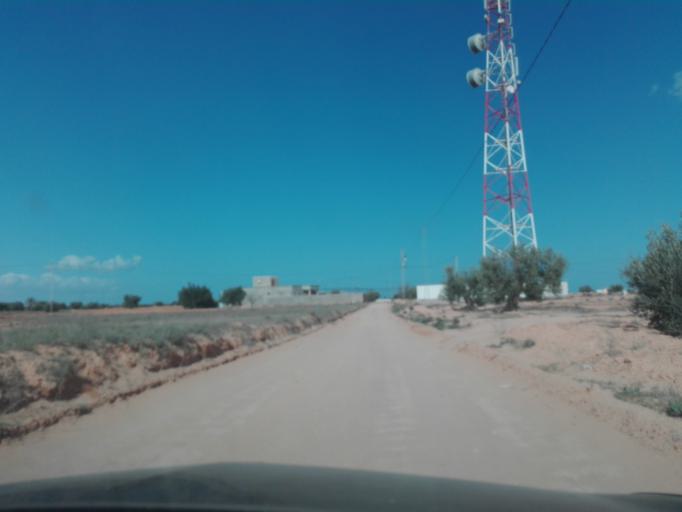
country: TN
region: Madanin
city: Bin Qirdan
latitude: 33.1684
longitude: 11.1968
